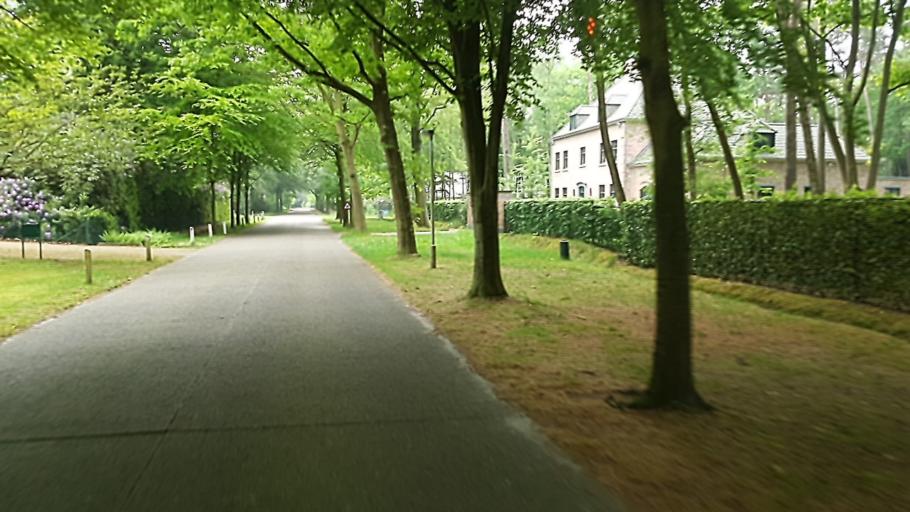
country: BE
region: Flanders
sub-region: Provincie Antwerpen
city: Kapellen
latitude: 51.3309
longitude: 4.4328
